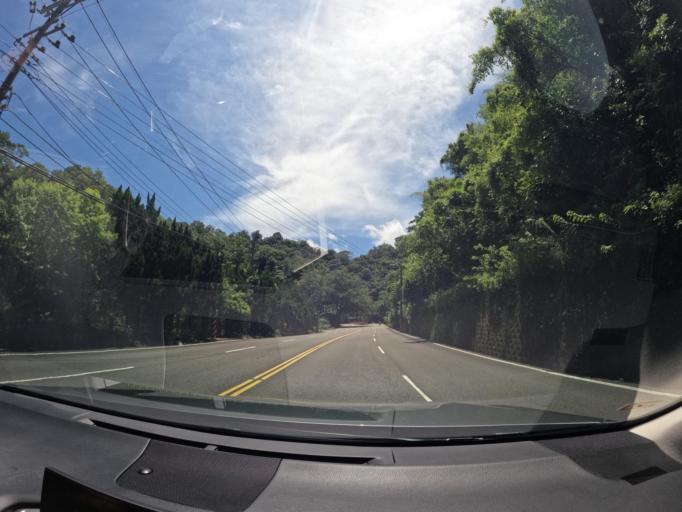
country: TW
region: Taiwan
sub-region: Miaoli
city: Miaoli
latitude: 24.5870
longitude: 120.9454
